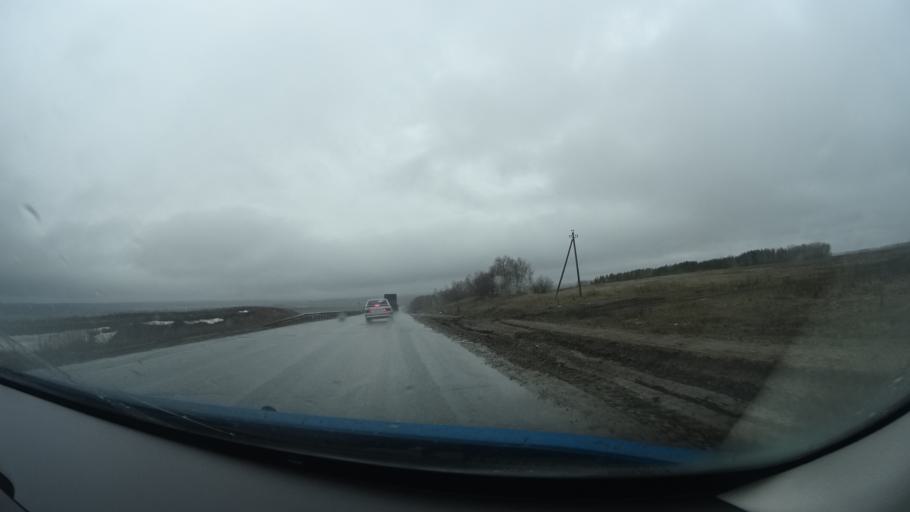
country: RU
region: Bashkortostan
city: Buzdyak
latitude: 54.6379
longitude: 54.4793
